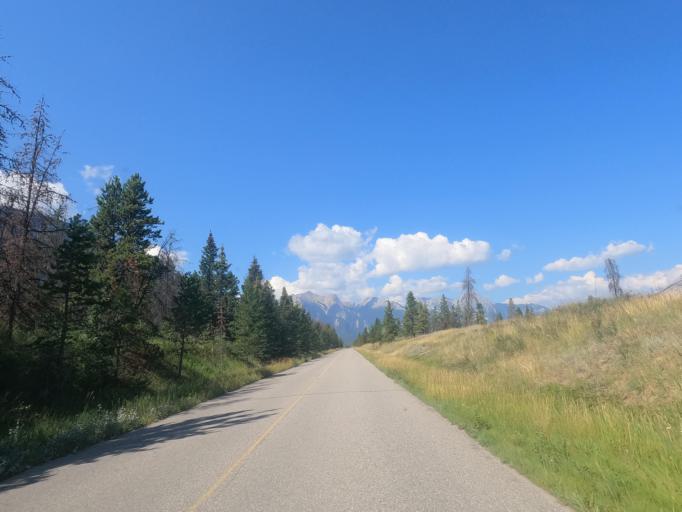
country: CA
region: Alberta
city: Jasper Park Lodge
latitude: 52.9742
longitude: -118.0628
